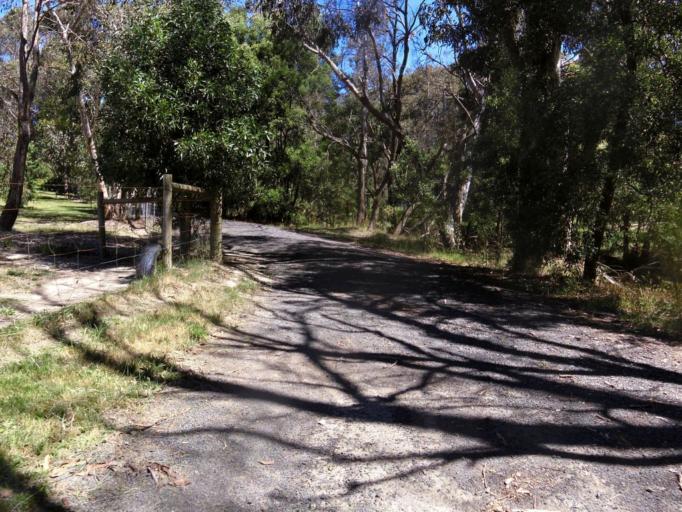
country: AU
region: Victoria
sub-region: Whittlesea
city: Whittlesea
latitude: -37.3649
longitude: 145.0358
